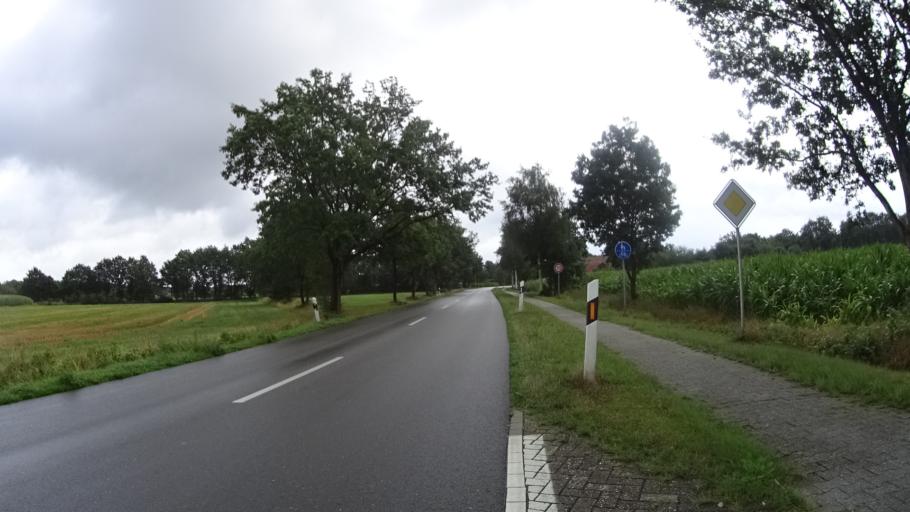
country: DE
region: Lower Saxony
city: Schwerinsdorf
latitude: 53.3437
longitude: 7.7478
